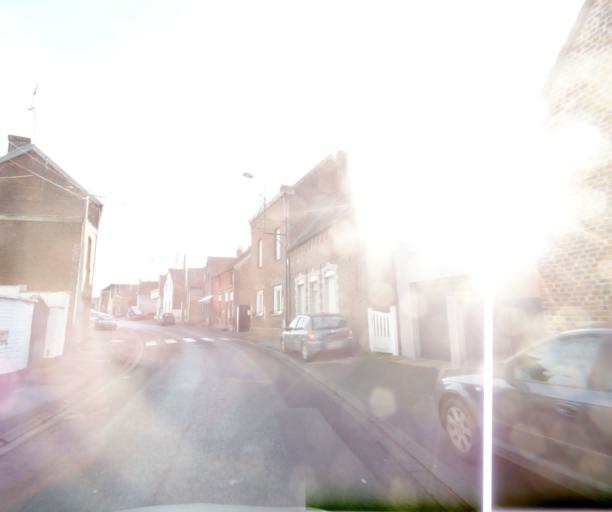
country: FR
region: Nord-Pas-de-Calais
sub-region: Departement du Nord
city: Maing
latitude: 50.3080
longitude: 3.4860
